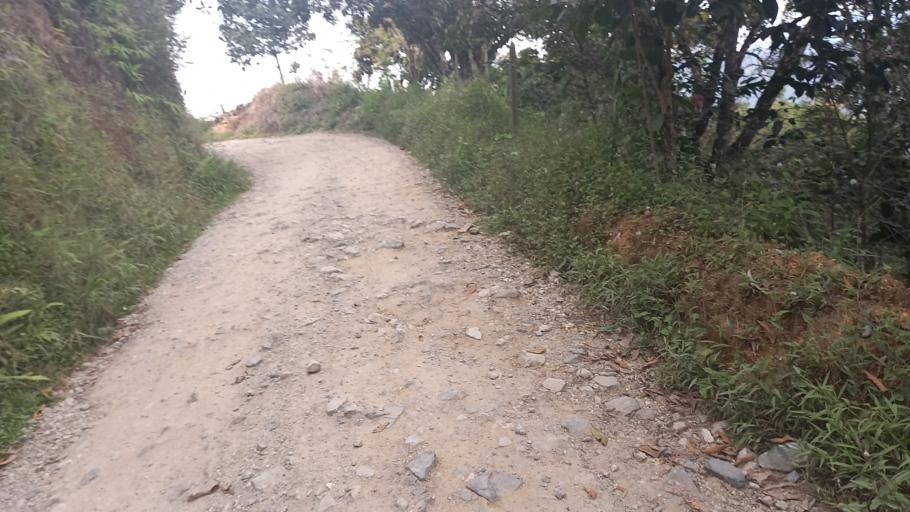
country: CO
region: Antioquia
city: Santa Barbara
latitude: 5.8340
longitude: -75.5759
